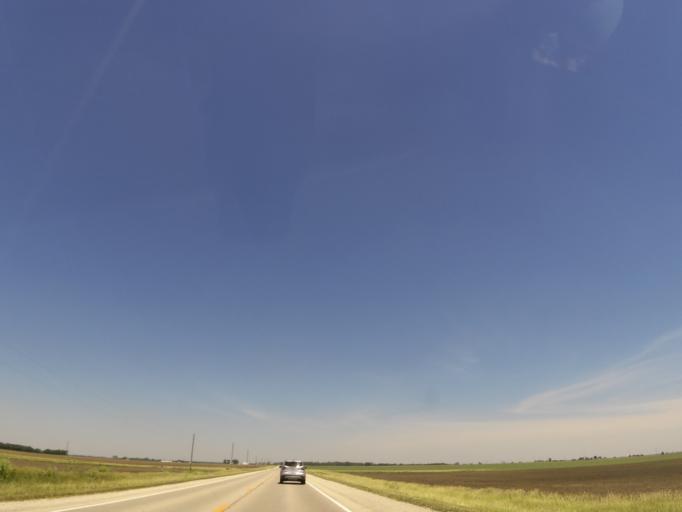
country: US
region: Illinois
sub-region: Vermilion County
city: Hoopeston
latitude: 40.5433
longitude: -87.6928
